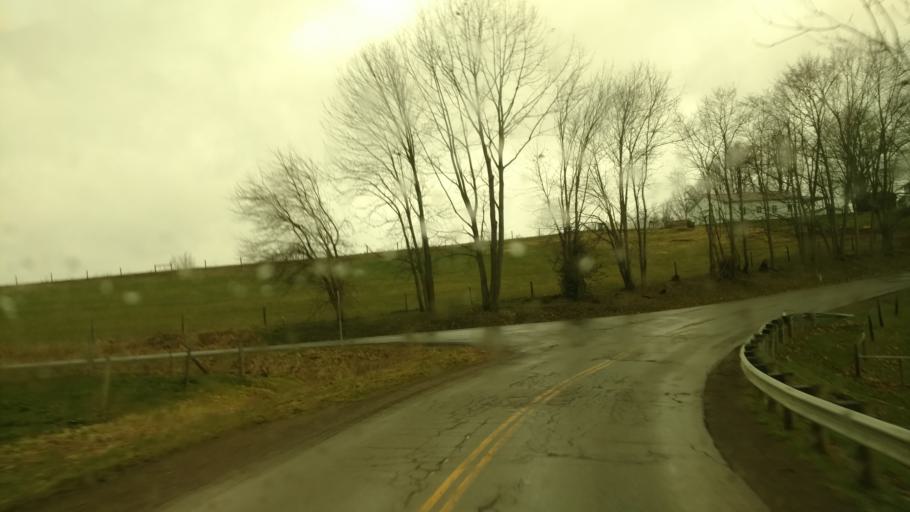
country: US
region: Ohio
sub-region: Holmes County
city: Millersburg
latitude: 40.5207
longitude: -81.8511
